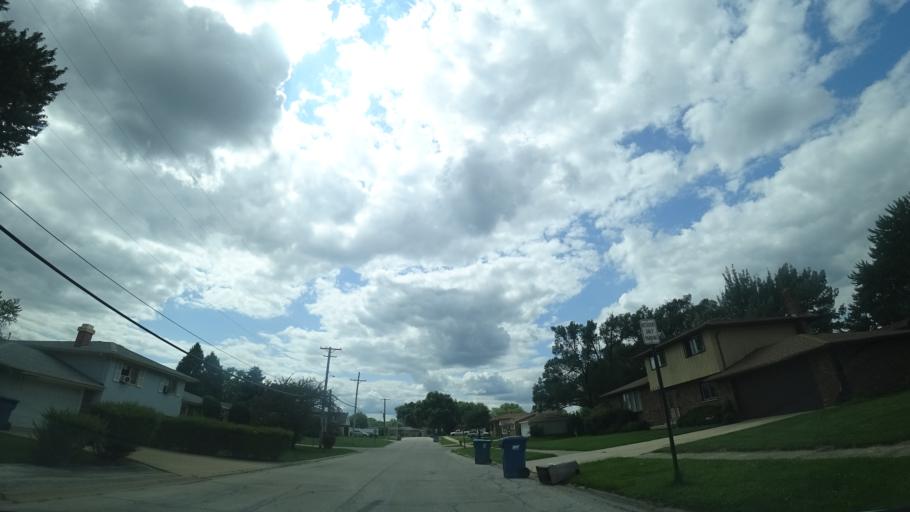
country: US
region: Illinois
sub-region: Cook County
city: Alsip
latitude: 41.6820
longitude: -87.7242
